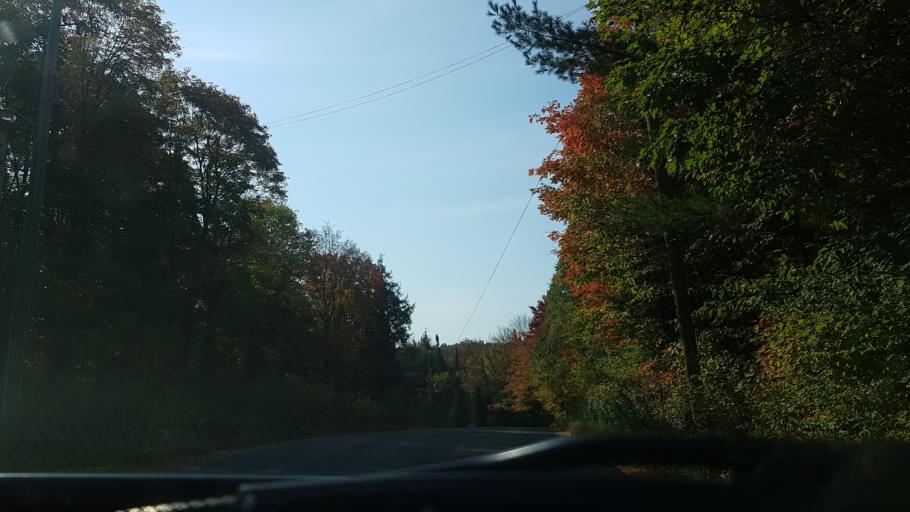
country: CA
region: Ontario
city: Bracebridge
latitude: 44.9424
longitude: -79.2427
